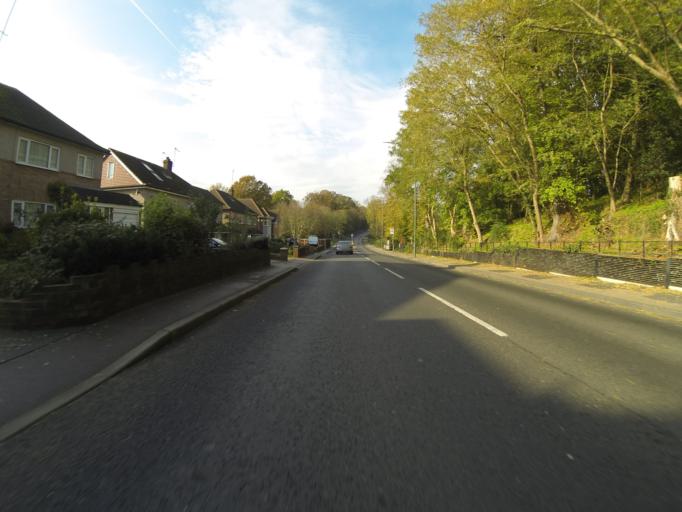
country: GB
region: England
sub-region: Greater London
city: Bexley
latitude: 51.4524
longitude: 0.1697
